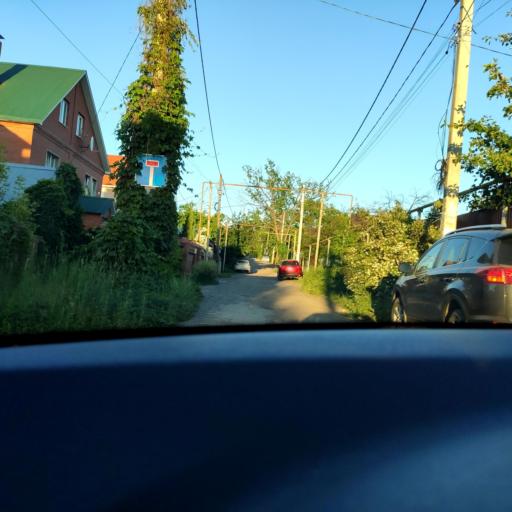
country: RU
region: Samara
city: Samara
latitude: 53.2728
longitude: 50.2160
